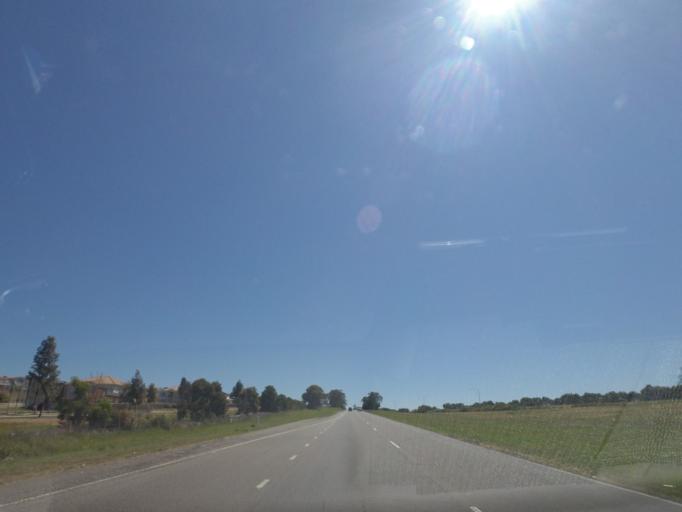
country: AU
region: Victoria
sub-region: Hume
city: Craigieburn
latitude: -37.5750
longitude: 144.9393
